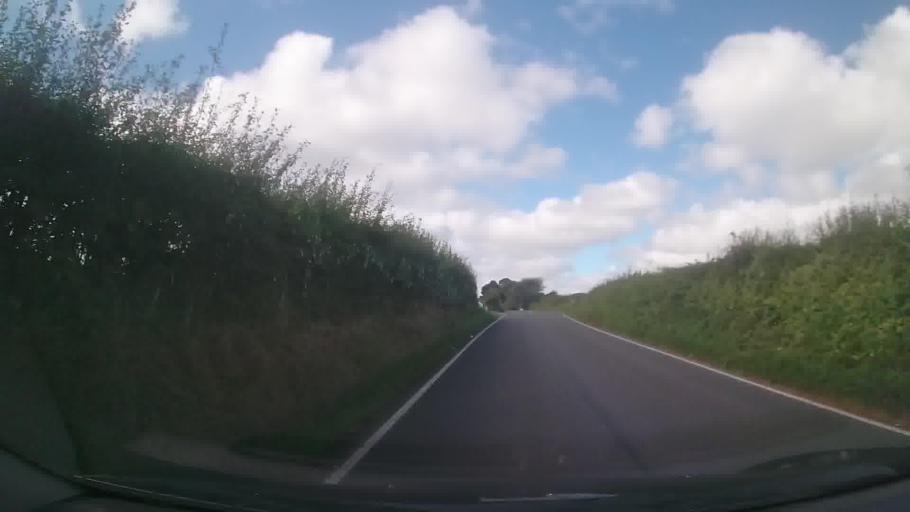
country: GB
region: Wales
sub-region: Pembrokeshire
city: Penally
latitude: 51.6569
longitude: -4.7451
